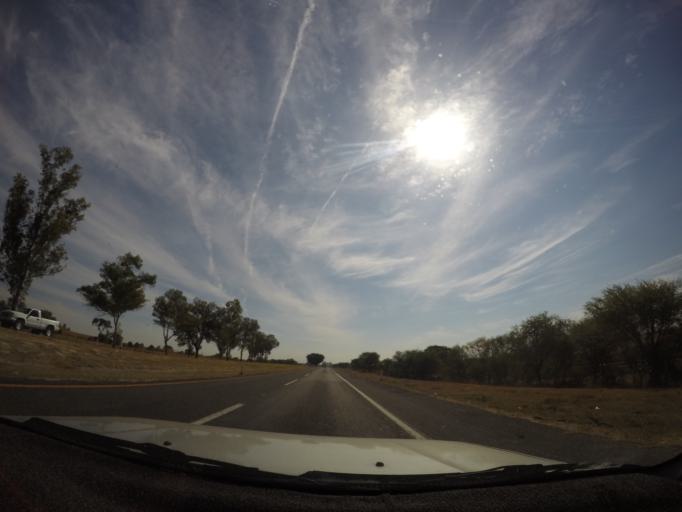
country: MX
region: Jalisco
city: La Barca
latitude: 20.3219
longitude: -102.5232
